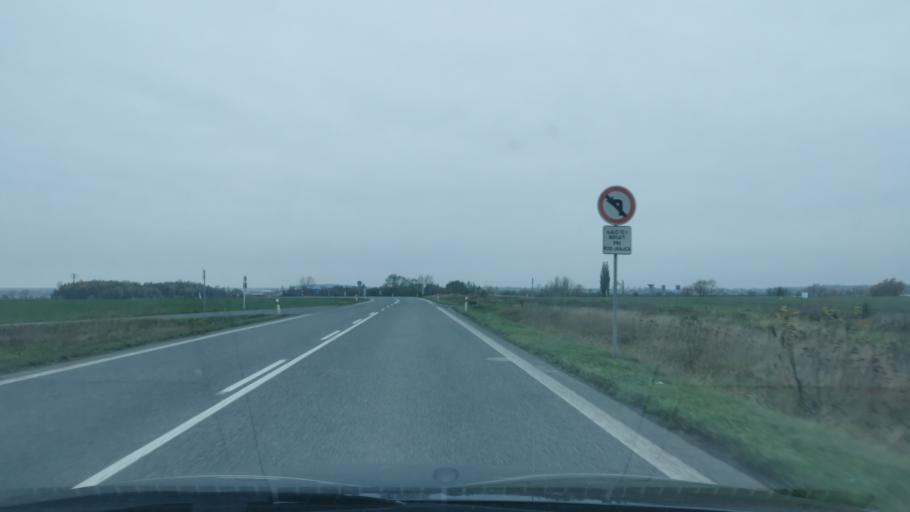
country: SK
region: Trnavsky
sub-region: Okres Skalica
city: Skalica
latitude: 48.8429
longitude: 17.2108
